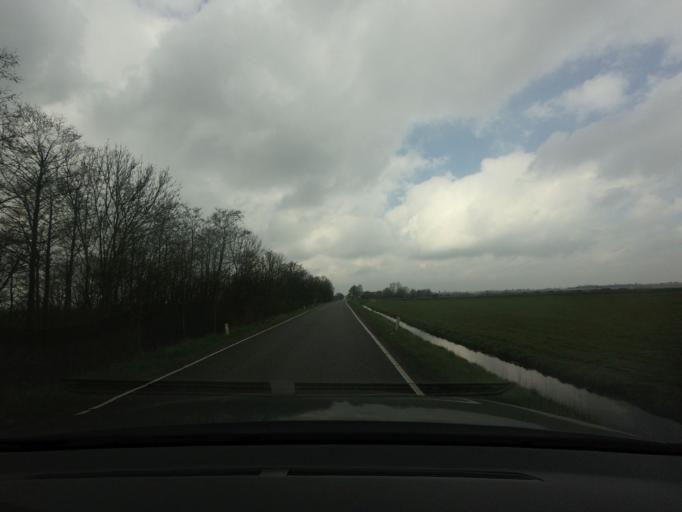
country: NL
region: South Holland
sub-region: Gemeente Nieuwkoop
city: Nieuwkoop
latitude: 52.1705
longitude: 4.8233
